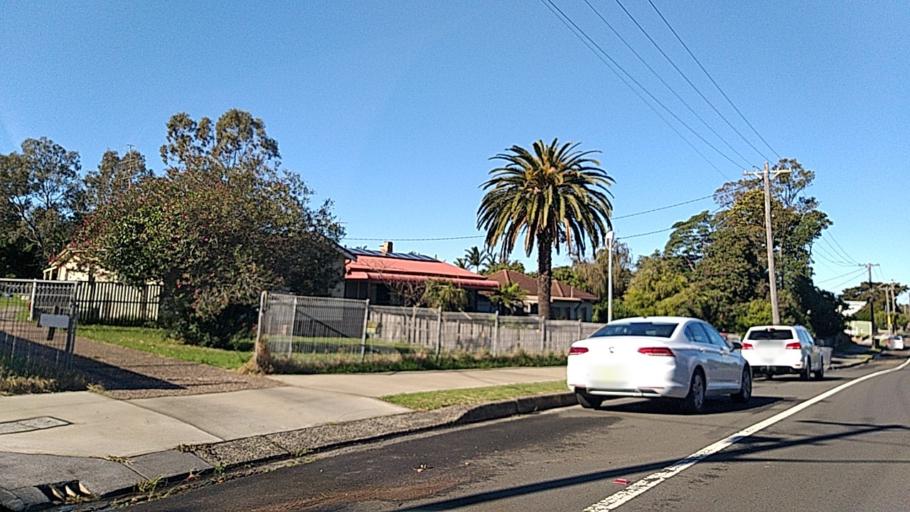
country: AU
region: New South Wales
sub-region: Wollongong
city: Berkeley
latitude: -34.4802
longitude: 150.8550
